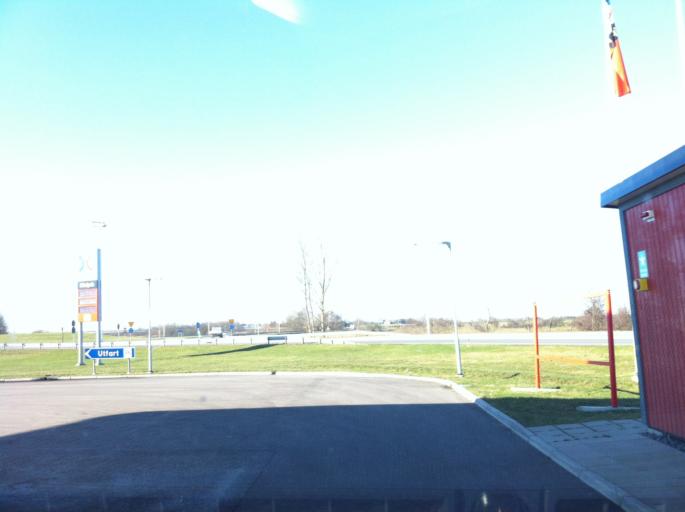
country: SE
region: Skane
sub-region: Svedala Kommun
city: Klagerup
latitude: 55.6290
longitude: 13.2437
